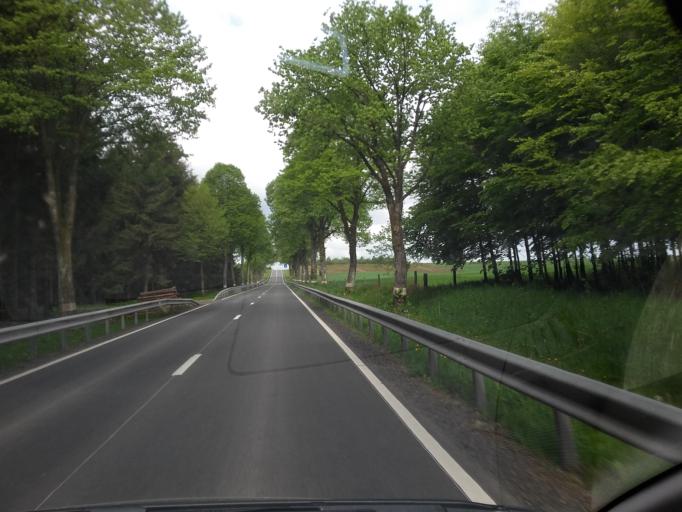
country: BE
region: Wallonia
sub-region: Province du Luxembourg
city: Neufchateau
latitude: 49.8416
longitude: 5.4047
